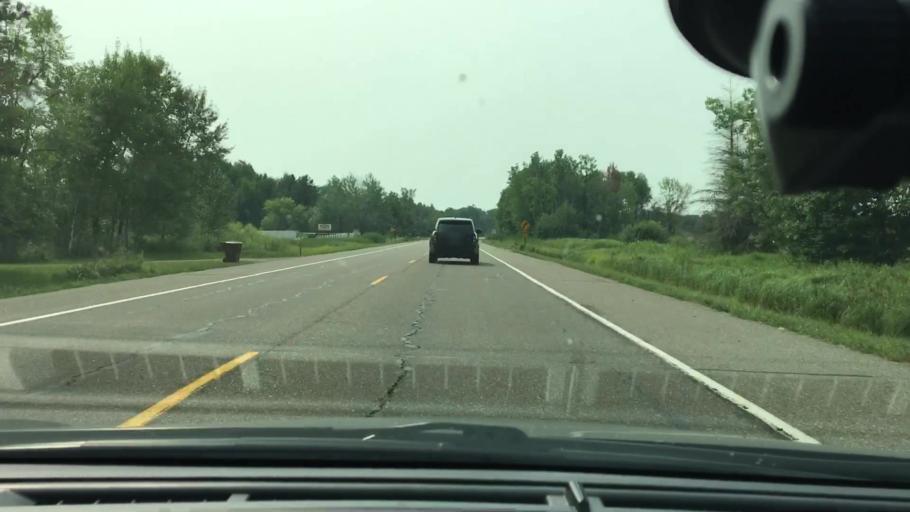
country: US
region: Minnesota
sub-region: Crow Wing County
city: Brainerd
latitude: 46.3892
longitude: -94.2233
